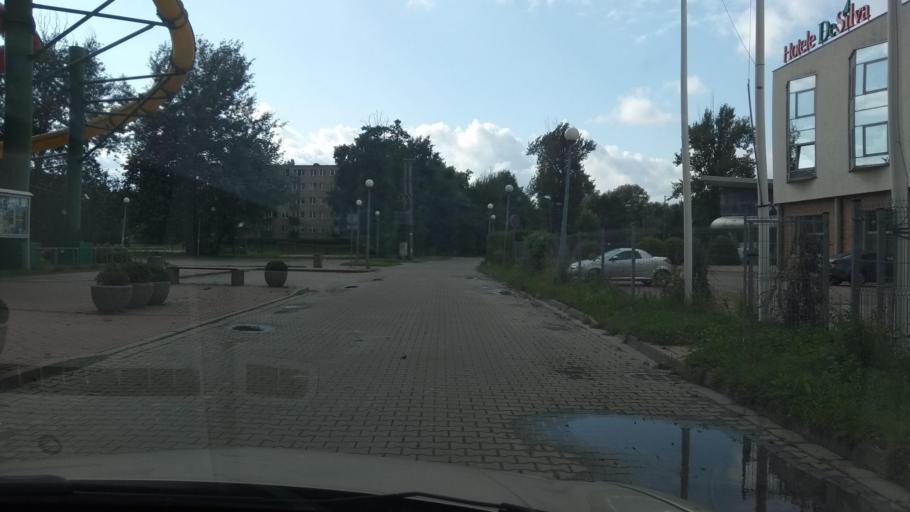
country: PL
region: Masovian Voivodeship
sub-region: Powiat pruszkowski
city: Pruszkow
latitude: 52.1622
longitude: 20.8224
